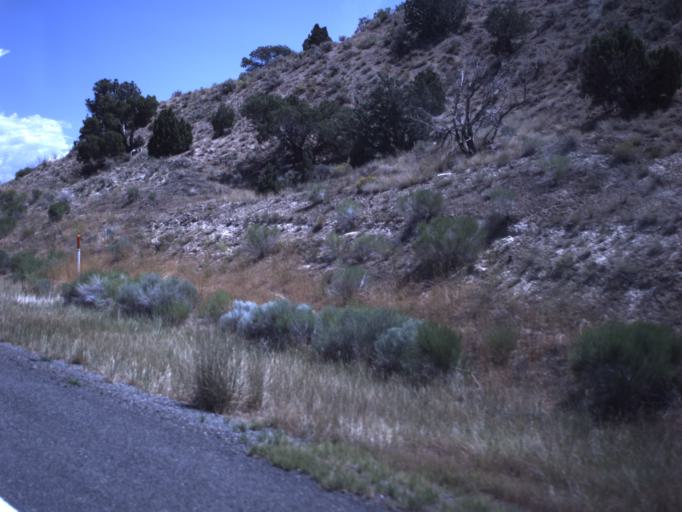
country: US
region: Utah
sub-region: Juab County
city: Nephi
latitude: 39.5746
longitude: -112.1854
